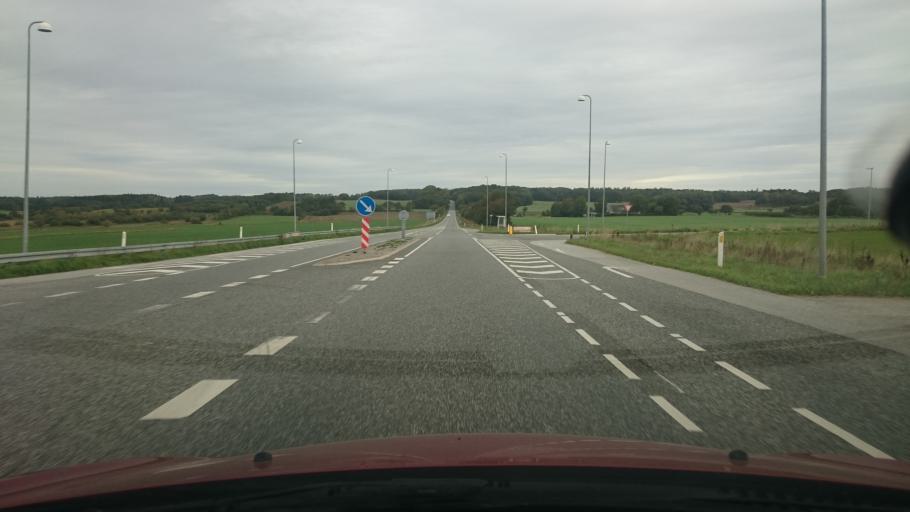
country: DK
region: North Denmark
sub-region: Mariagerfjord Kommune
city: Hadsund
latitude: 56.6459
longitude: 10.1615
